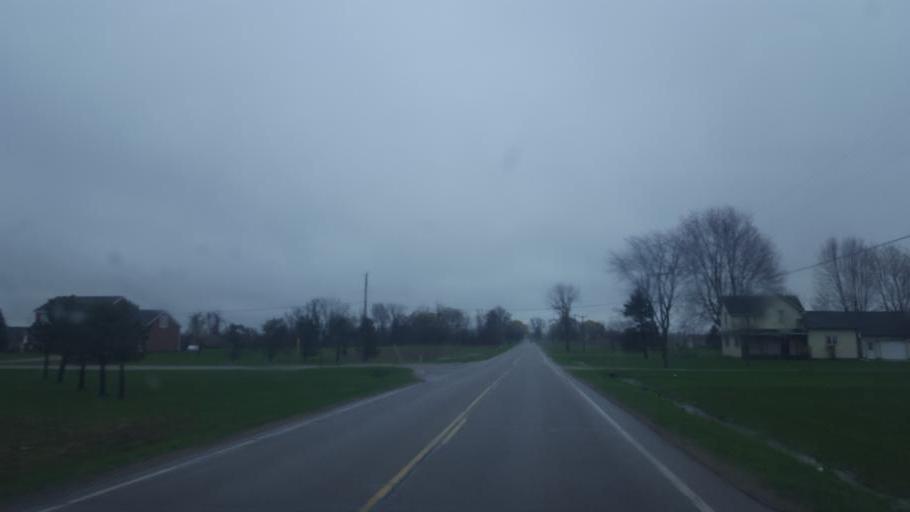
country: US
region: Michigan
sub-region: Isabella County
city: Mount Pleasant
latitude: 43.6114
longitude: -84.8314
